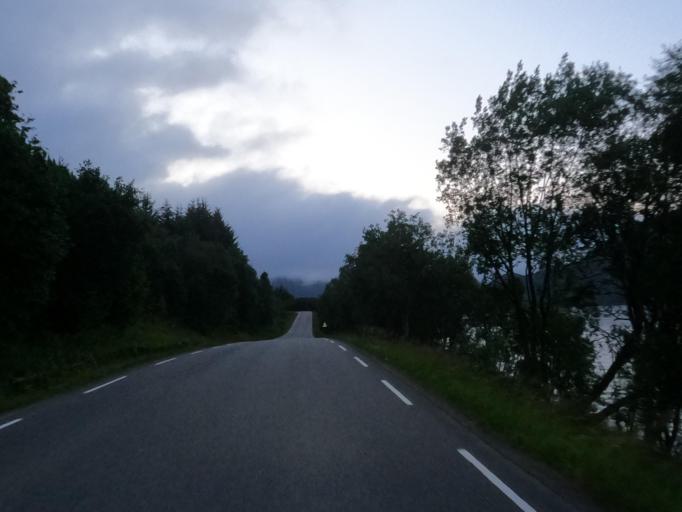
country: NO
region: Nordland
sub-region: Lodingen
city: Lodingen
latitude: 68.5957
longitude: 15.7883
